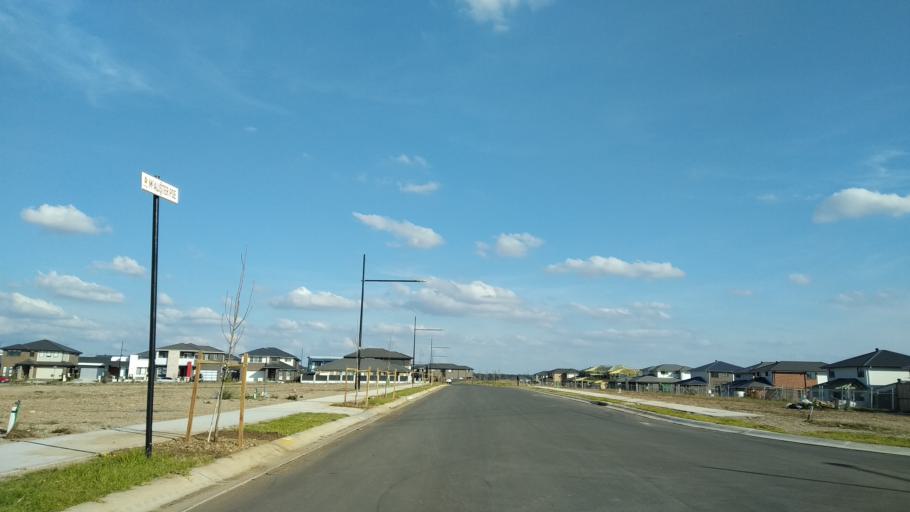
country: AU
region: New South Wales
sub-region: Blacktown
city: Blackett
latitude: -33.6905
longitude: 150.8089
